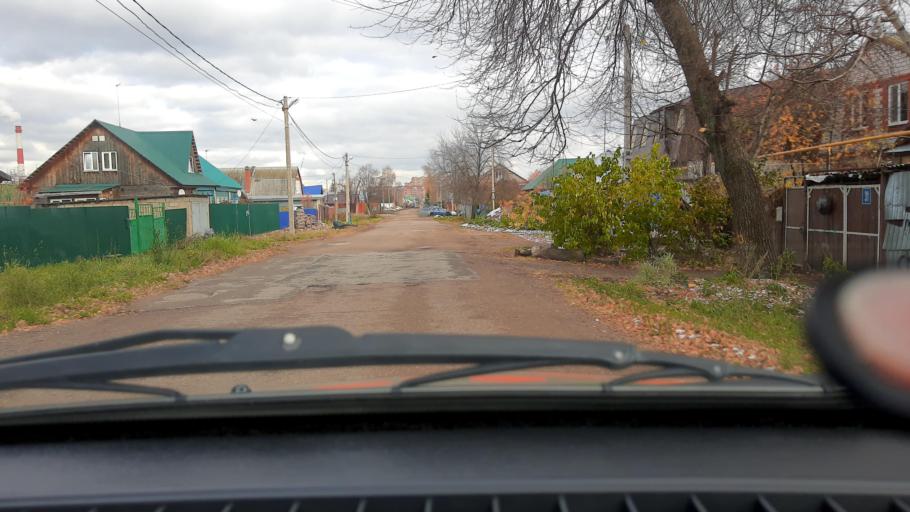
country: RU
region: Bashkortostan
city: Ufa
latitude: 54.7800
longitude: 56.0587
